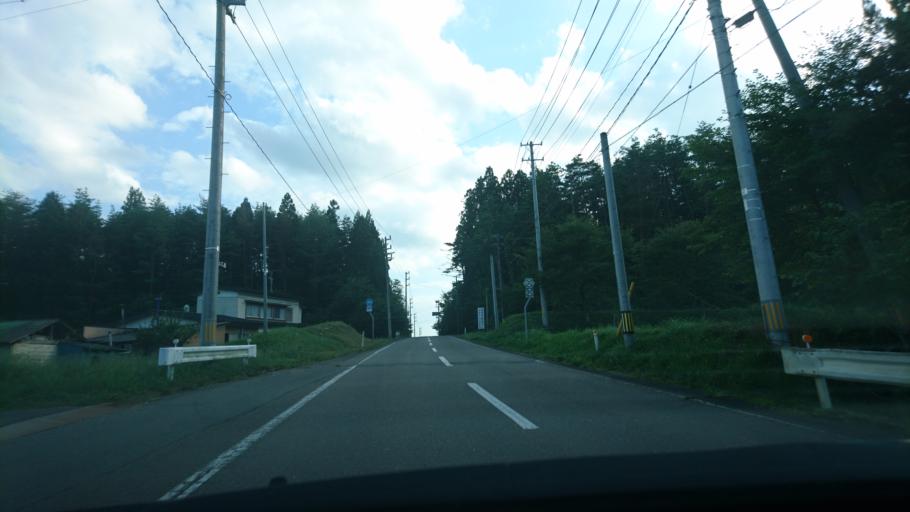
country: JP
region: Iwate
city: Ichinoseki
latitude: 39.0104
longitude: 141.2866
